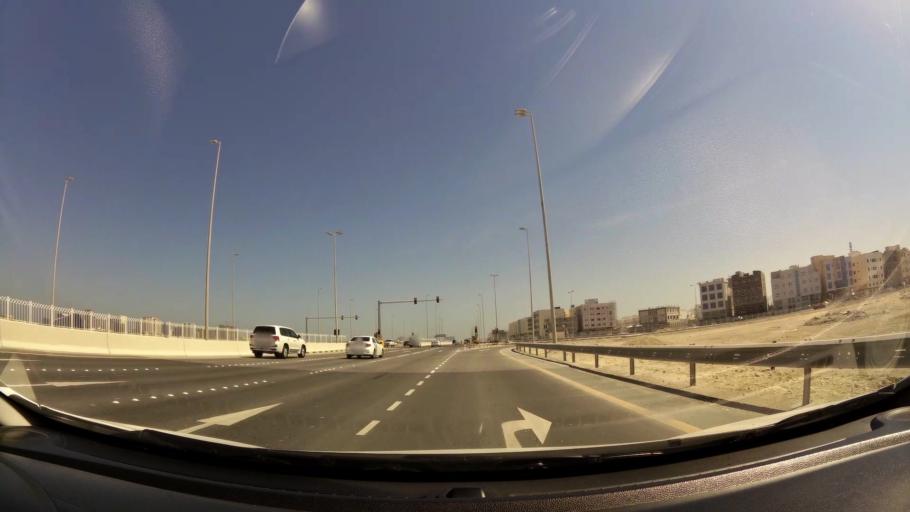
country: BH
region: Muharraq
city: Al Hadd
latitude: 26.2841
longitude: 50.6444
